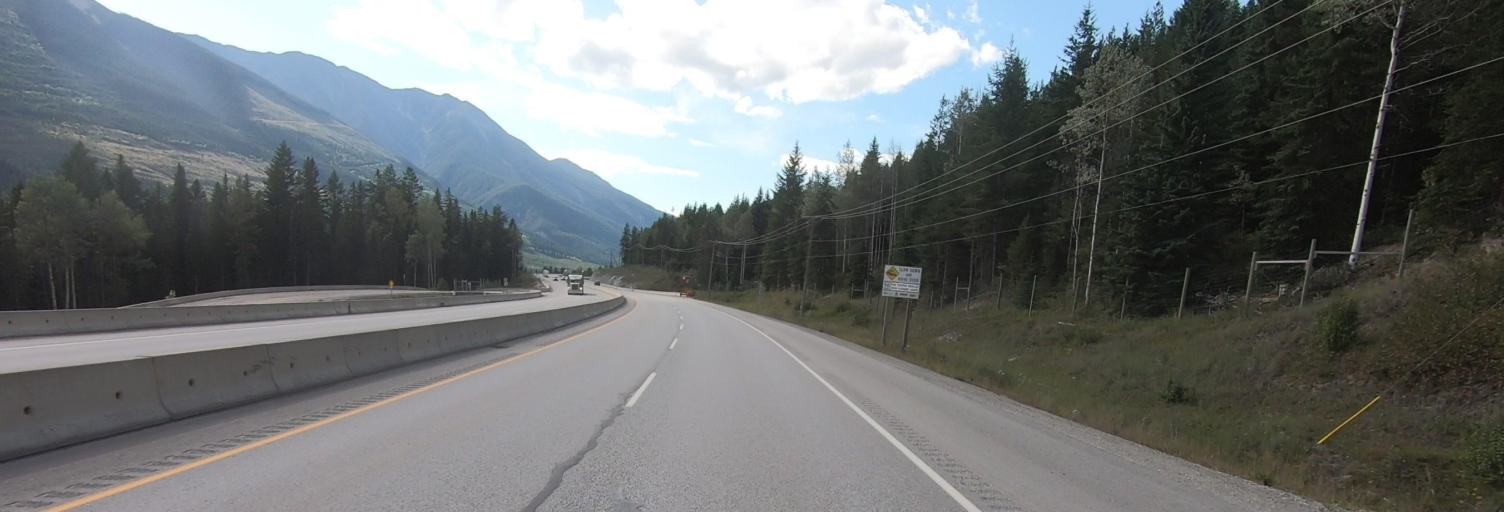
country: CA
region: British Columbia
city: Golden
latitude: 51.2586
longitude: -116.7029
